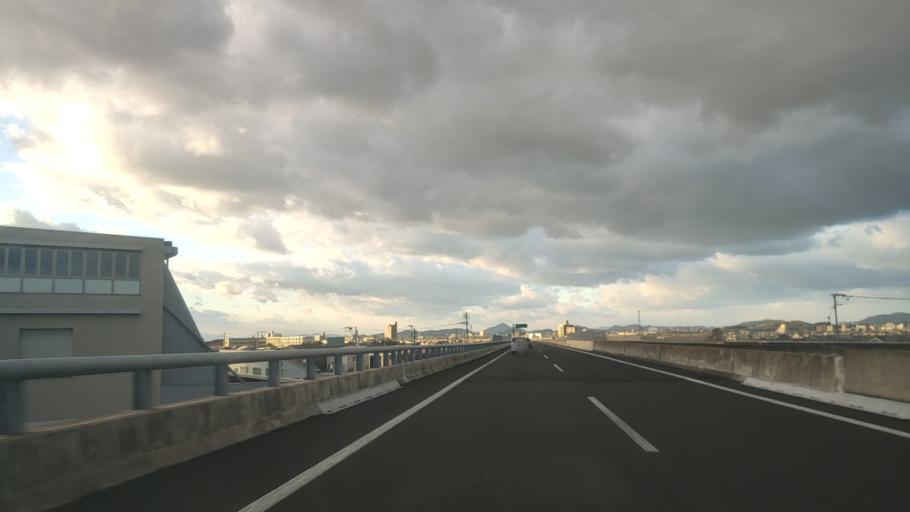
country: JP
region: Ehime
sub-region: Shikoku-chuo Shi
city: Matsuyama
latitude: 33.7904
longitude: 132.8046
